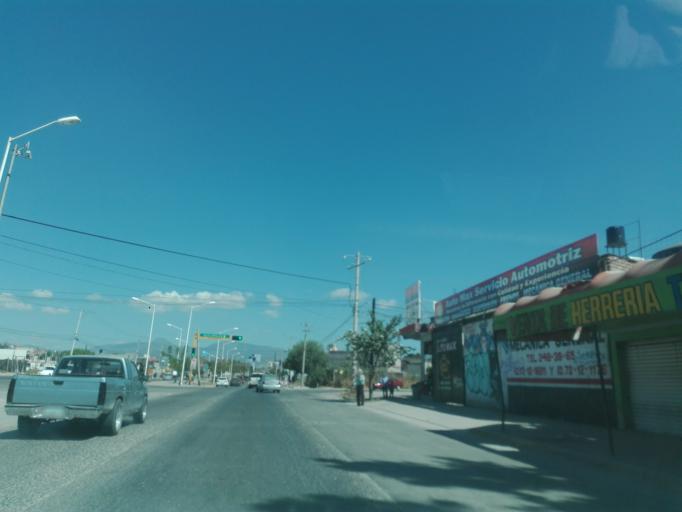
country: MX
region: Guanajuato
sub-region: Leon
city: San Jose de Duran (Los Troncoso)
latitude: 21.0762
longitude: -101.6355
